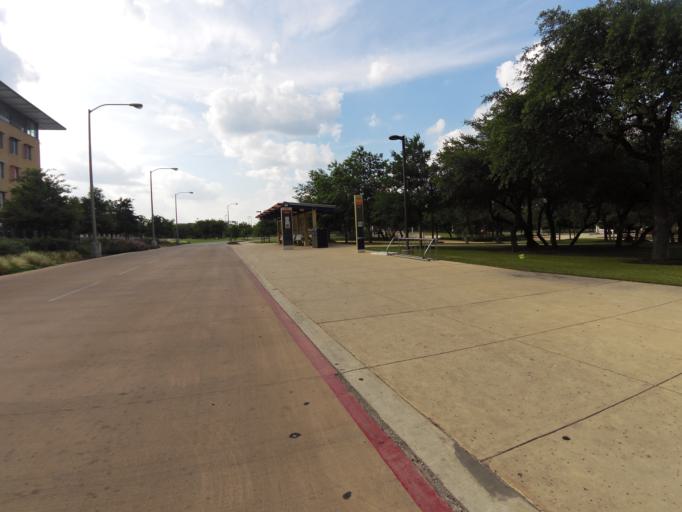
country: US
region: Texas
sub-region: Bexar County
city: Shavano Park
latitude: 29.5858
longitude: -98.6191
